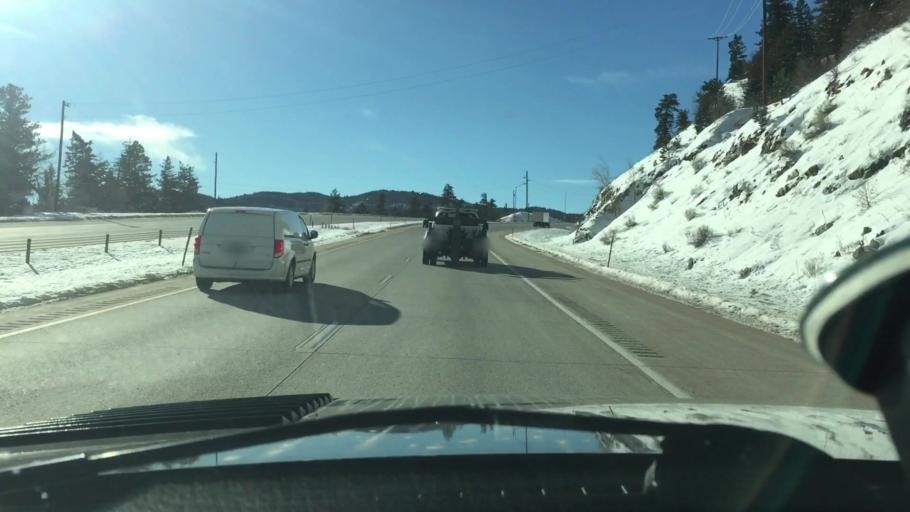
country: US
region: Colorado
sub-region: Jefferson County
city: Indian Hills
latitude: 39.5594
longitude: -105.2397
